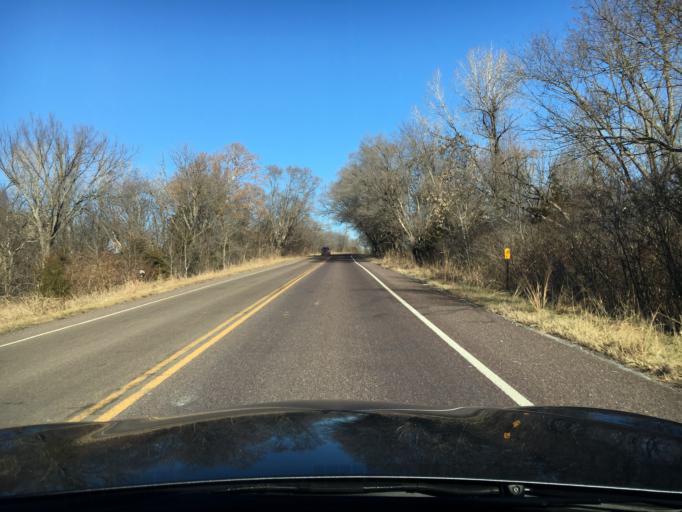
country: US
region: Missouri
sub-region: Cass County
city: Belton
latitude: 38.8181
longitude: -94.6670
